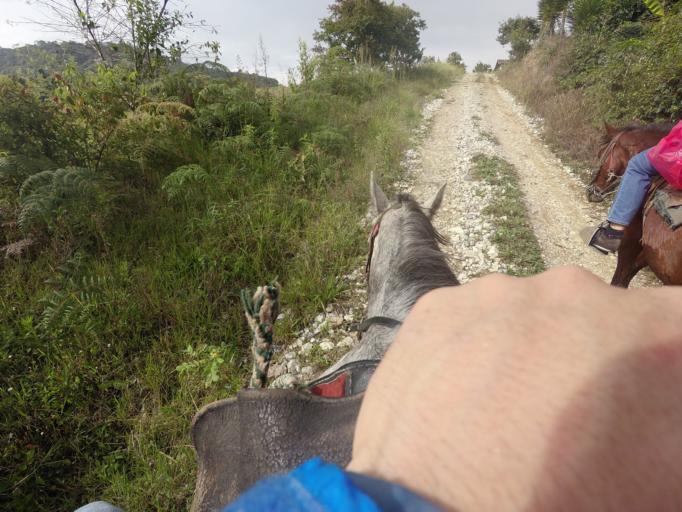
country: CO
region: Huila
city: San Agustin
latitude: 1.9101
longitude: -76.2918
